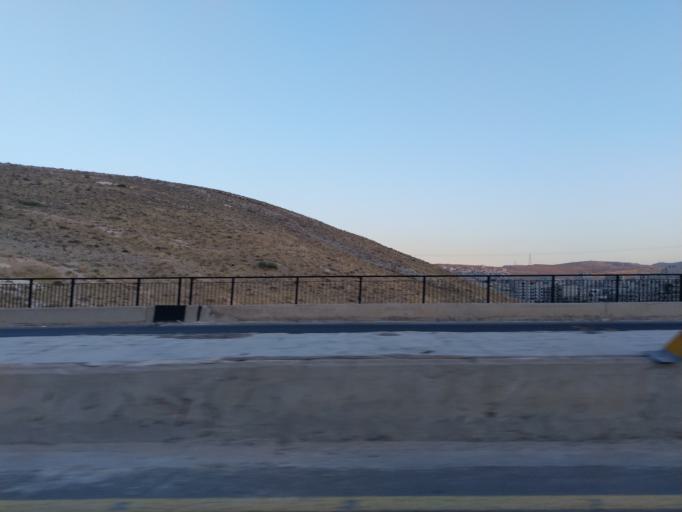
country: SY
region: Rif-dimashq
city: At Tall
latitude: 33.5860
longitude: 36.2937
